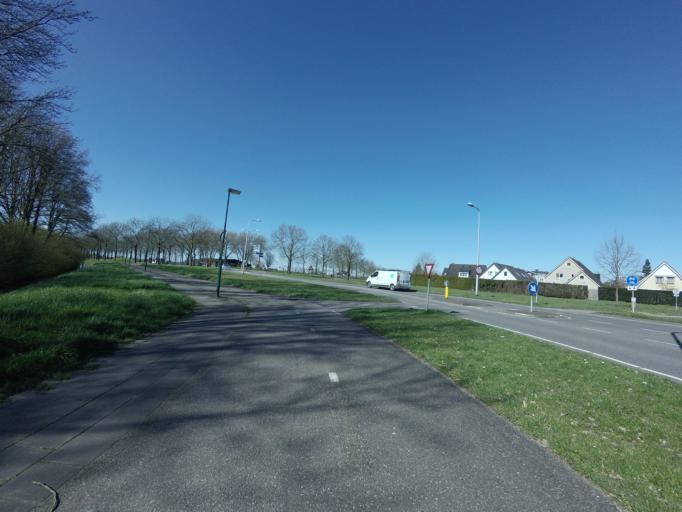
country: NL
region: Utrecht
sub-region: Gemeente Wijk bij Duurstede
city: Wijk bij Duurstede
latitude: 51.9795
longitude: 5.3312
